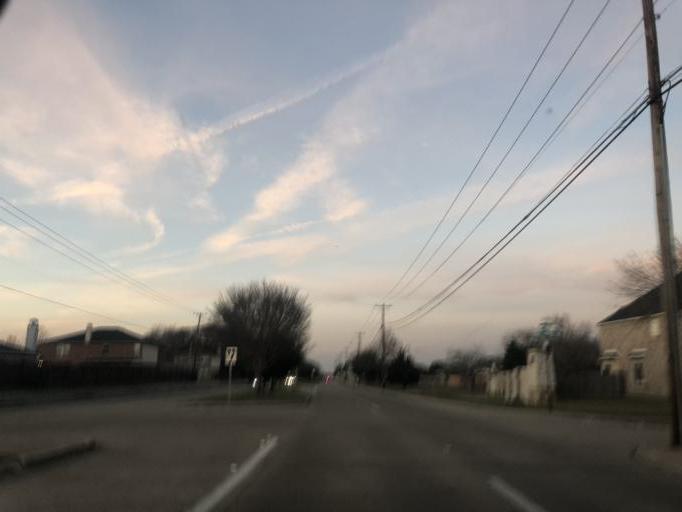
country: US
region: Texas
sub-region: Dallas County
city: Cedar Hill
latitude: 32.5975
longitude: -96.9253
